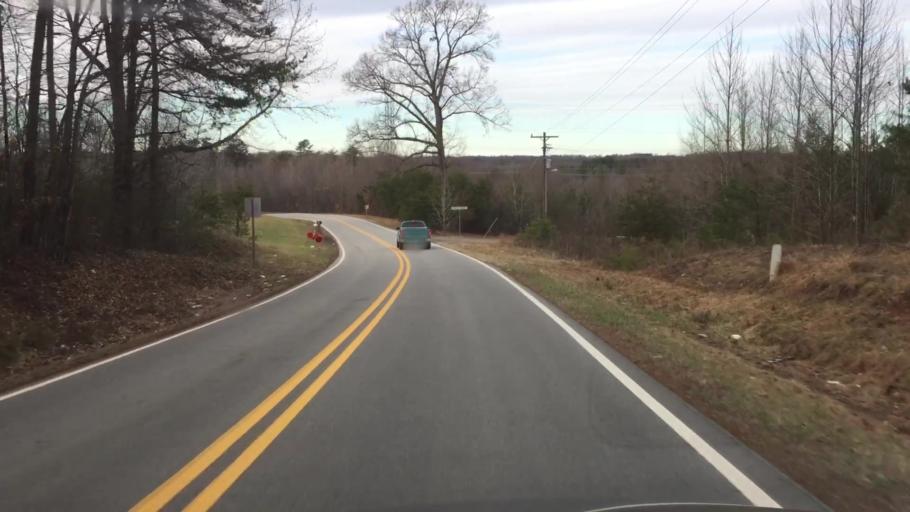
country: US
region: North Carolina
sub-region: Rockingham County
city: Reidsville
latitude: 36.3928
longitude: -79.6565
